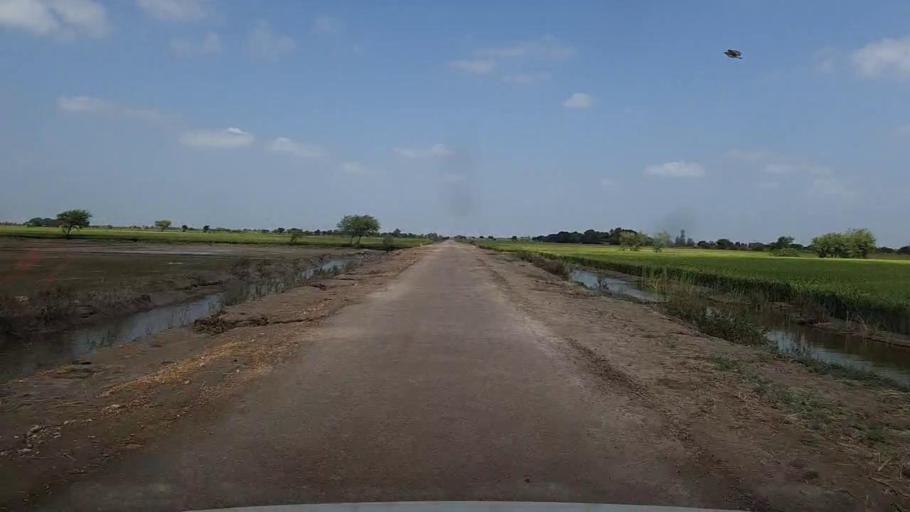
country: PK
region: Sindh
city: Kario
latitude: 24.6831
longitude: 68.5880
